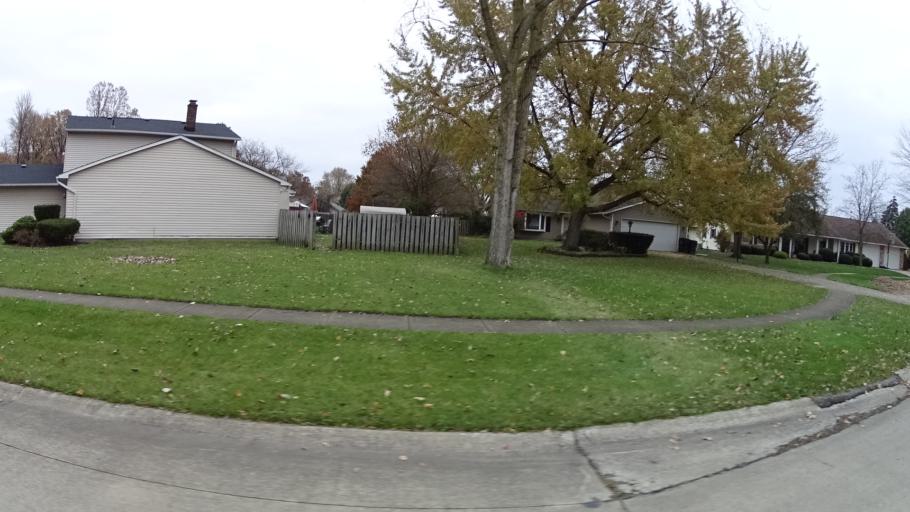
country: US
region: Ohio
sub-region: Lorain County
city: Sheffield
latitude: 41.4161
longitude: -82.0856
